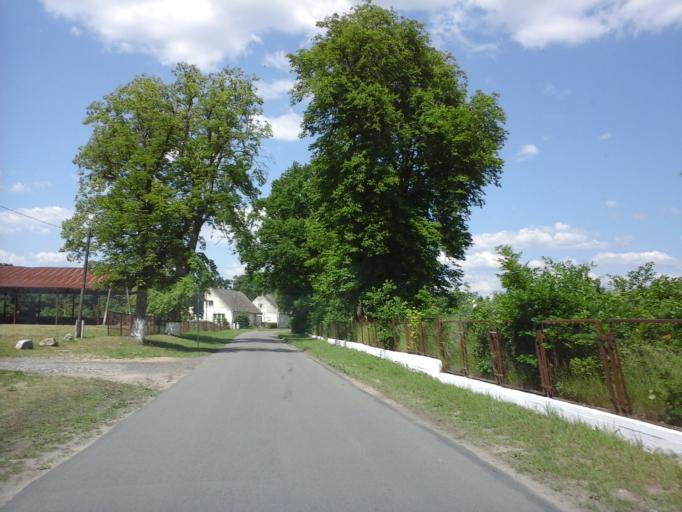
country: PL
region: West Pomeranian Voivodeship
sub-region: Powiat choszczenski
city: Bierzwnik
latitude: 53.1495
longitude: 15.6263
